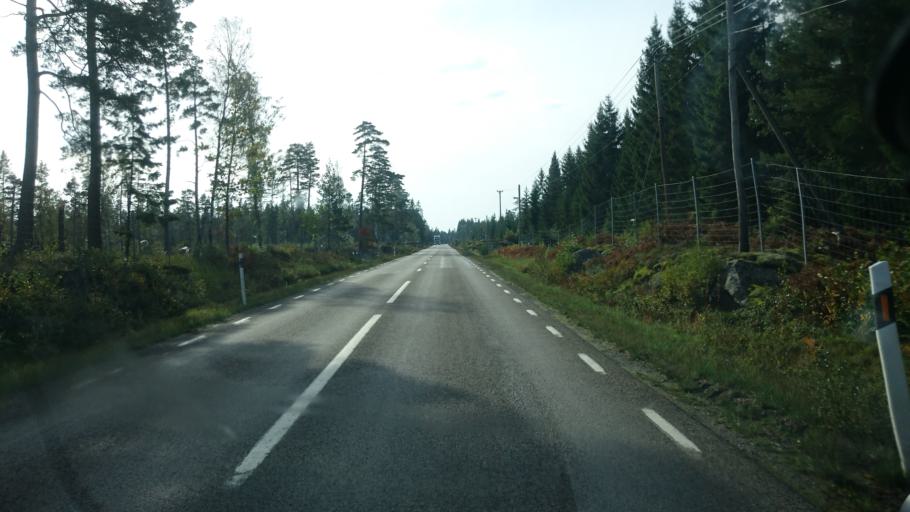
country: SE
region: Vaestra Goetaland
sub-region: Alingsas Kommun
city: Sollebrunn
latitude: 58.1999
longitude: 12.4308
